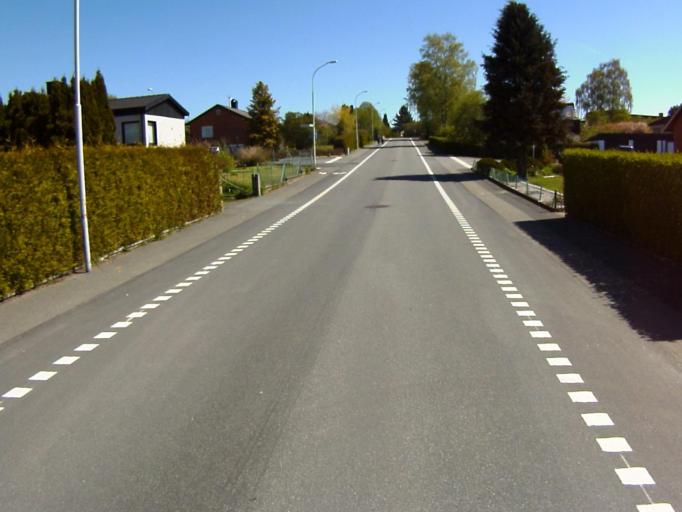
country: SE
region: Skane
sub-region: Kristianstads Kommun
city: Kristianstad
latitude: 56.0496
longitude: 14.2080
